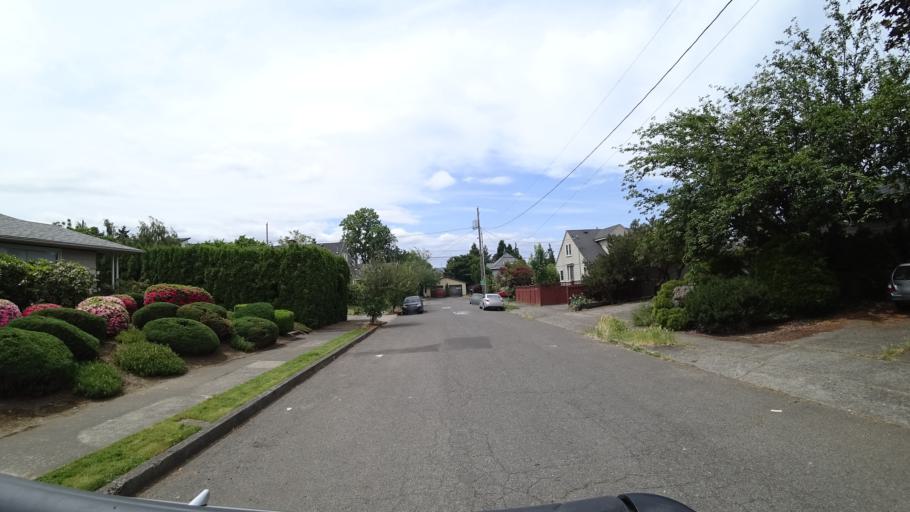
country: US
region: Oregon
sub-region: Multnomah County
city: Lents
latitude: 45.5242
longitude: -122.6036
